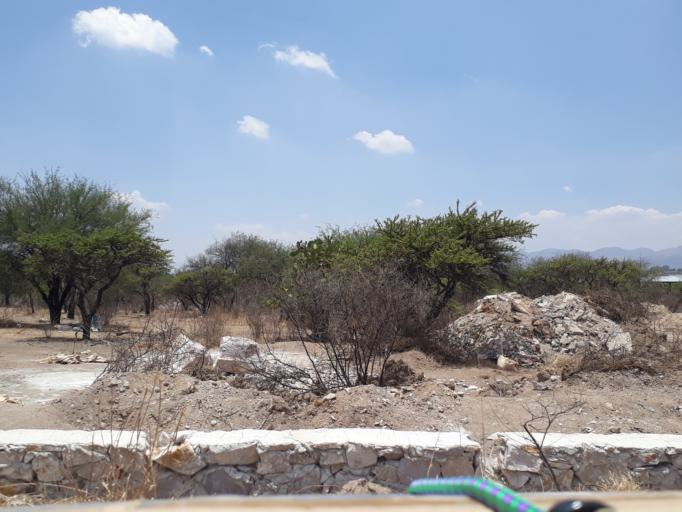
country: MX
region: Aguascalientes
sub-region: Aguascalientes
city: San Sebastian [Fraccionamiento]
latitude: 21.7793
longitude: -102.3305
